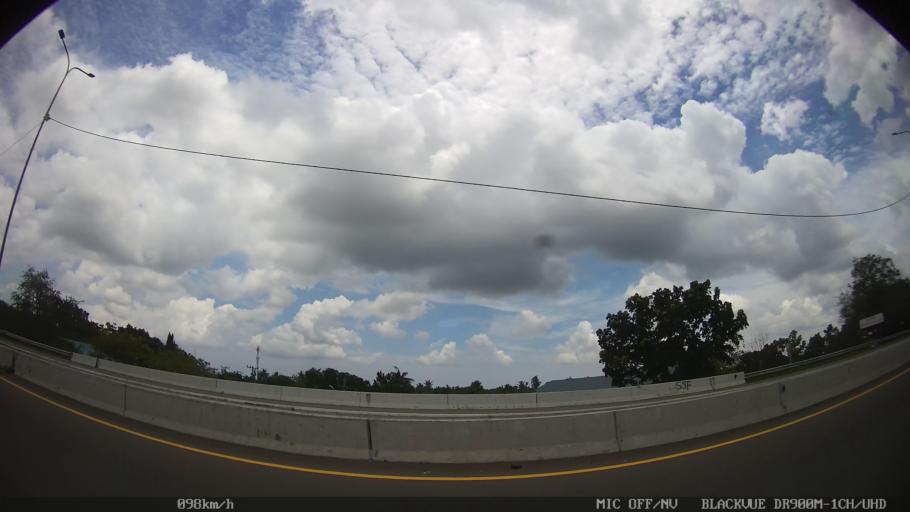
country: ID
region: North Sumatra
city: Medan
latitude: 3.6315
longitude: 98.7165
